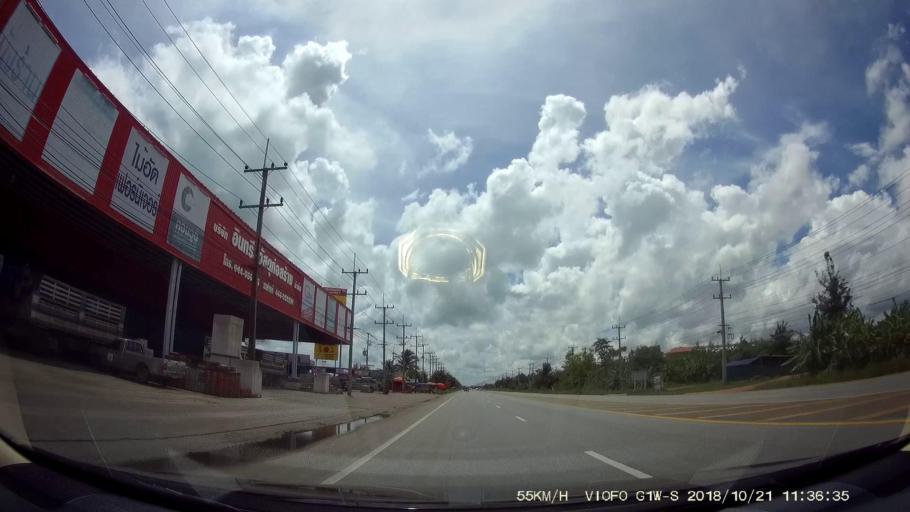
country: TH
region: Chaiyaphum
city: Chaiyaphum
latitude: 15.7181
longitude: 102.0161
